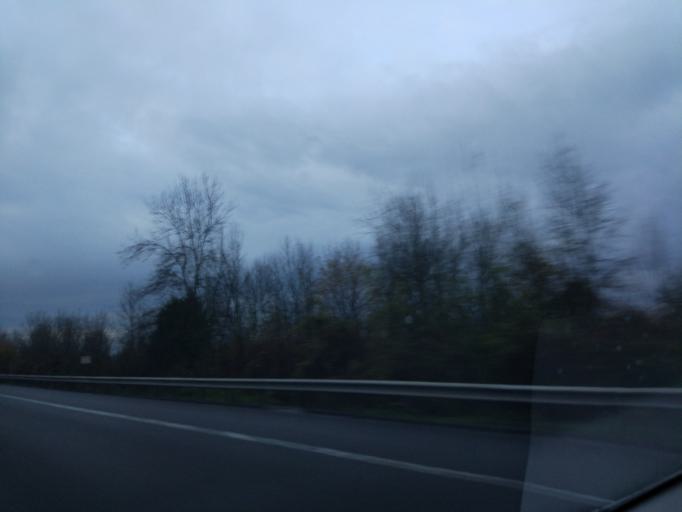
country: TR
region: Duzce
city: Duzce
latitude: 40.7952
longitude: 31.1975
